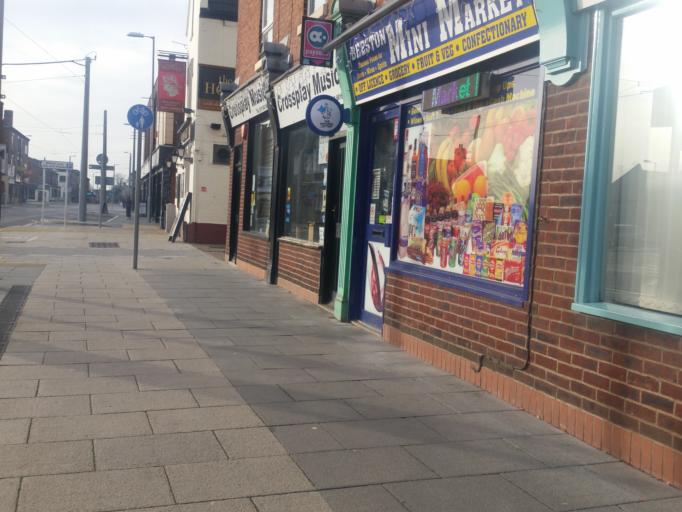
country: GB
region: England
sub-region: Derbyshire
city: Long Eaton
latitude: 52.9228
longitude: -1.2203
